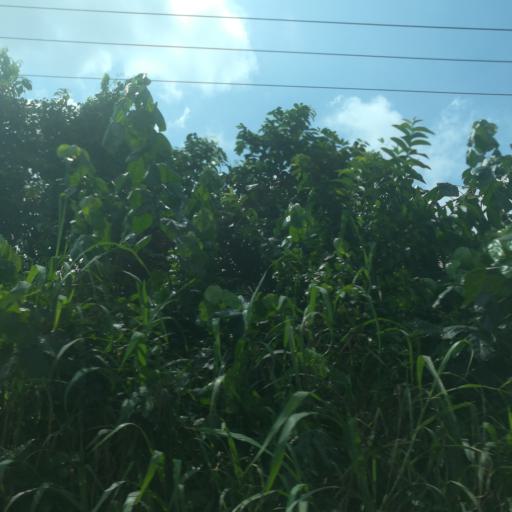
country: NG
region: Lagos
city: Ikorodu
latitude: 6.6690
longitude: 3.6432
